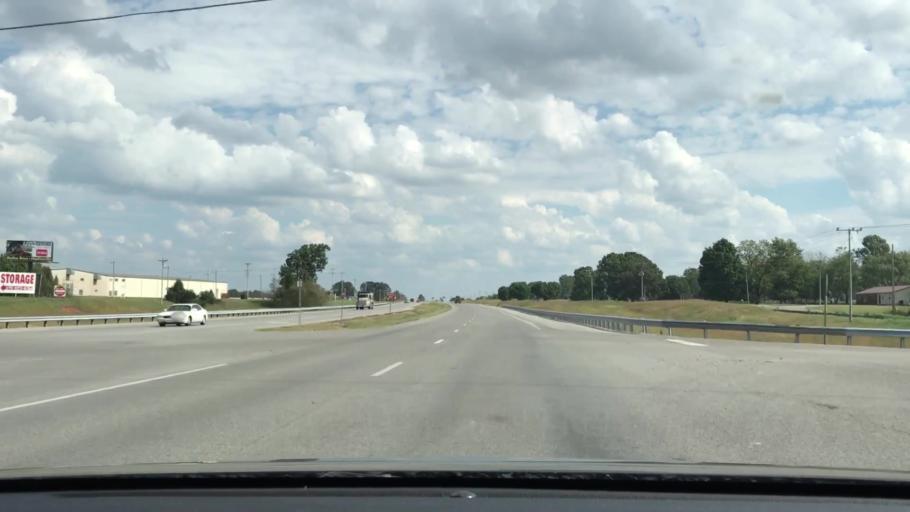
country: US
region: Kentucky
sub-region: Trigg County
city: Cadiz
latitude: 36.8712
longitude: -87.7653
